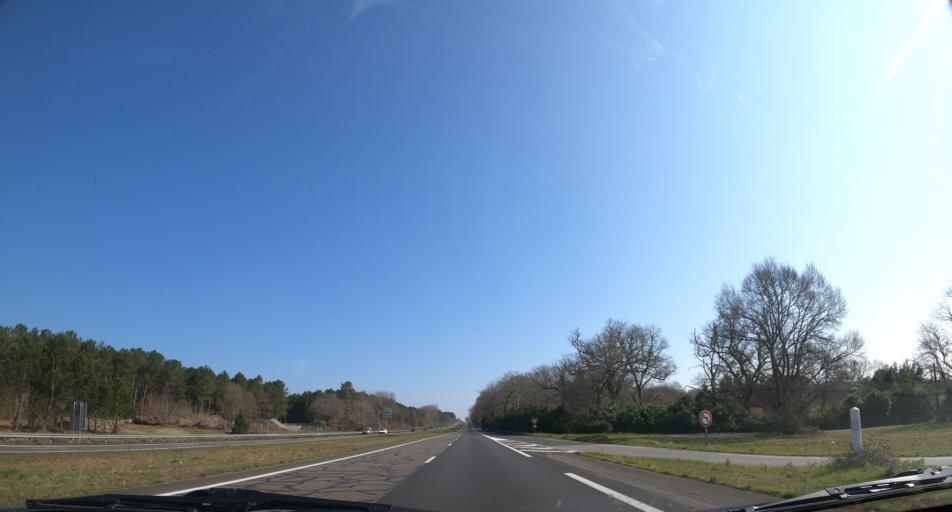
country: FR
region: Aquitaine
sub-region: Departement des Landes
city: Saint-Geours-de-Maremne
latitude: 43.6997
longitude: -1.1897
